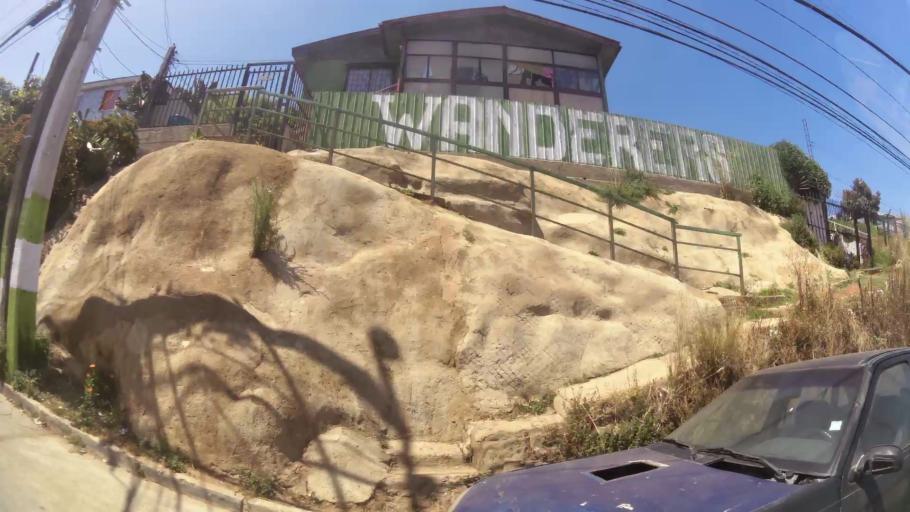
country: CL
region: Valparaiso
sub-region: Provincia de Valparaiso
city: Valparaiso
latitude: -33.0351
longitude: -71.6500
